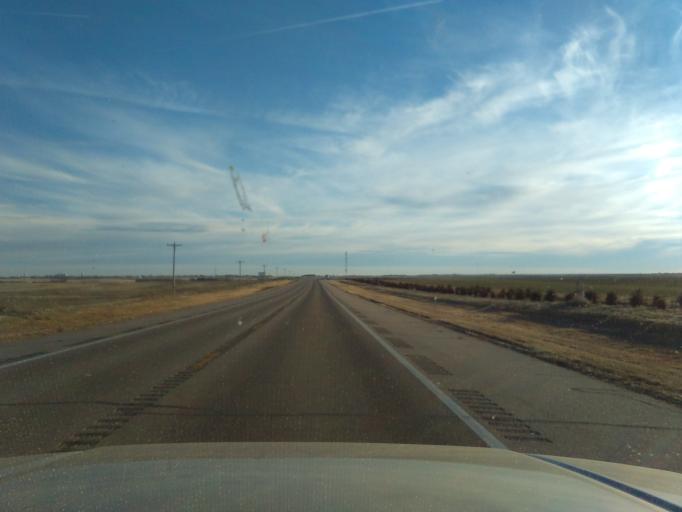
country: US
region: Kansas
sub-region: Logan County
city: Oakley
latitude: 39.1700
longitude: -100.8704
